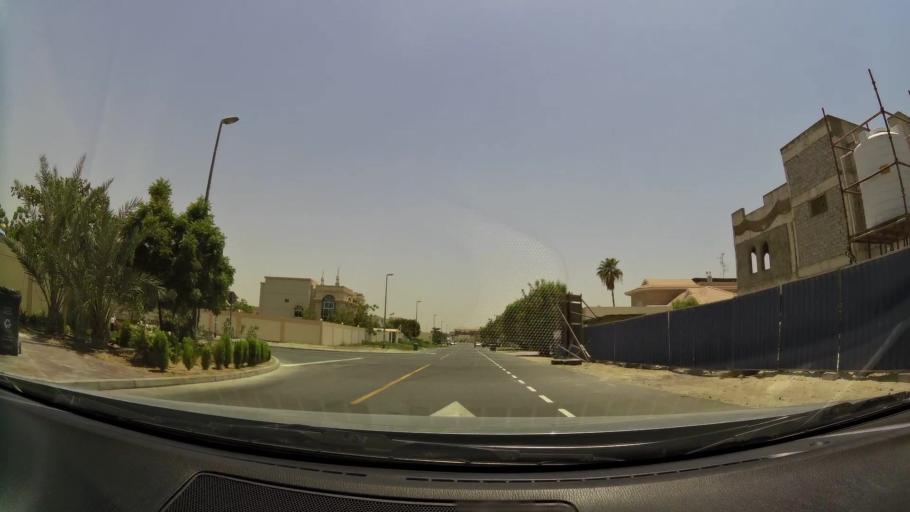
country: AE
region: Dubai
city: Dubai
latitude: 25.0954
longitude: 55.1995
